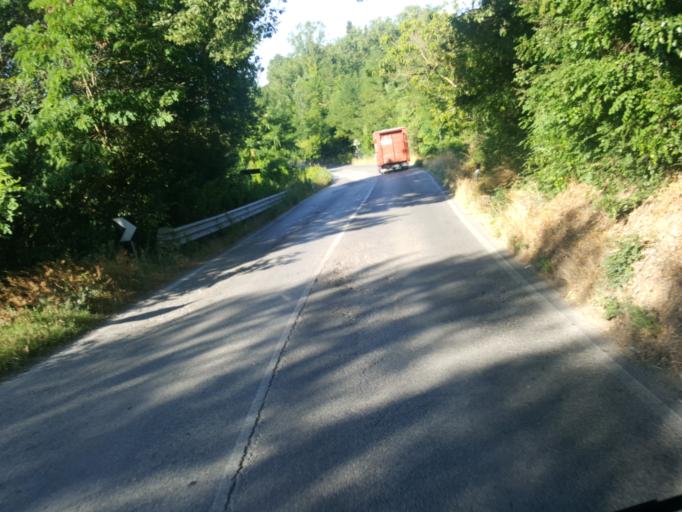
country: IT
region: The Marches
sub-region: Provincia di Pesaro e Urbino
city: Borgo Massano
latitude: 43.8125
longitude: 12.6633
